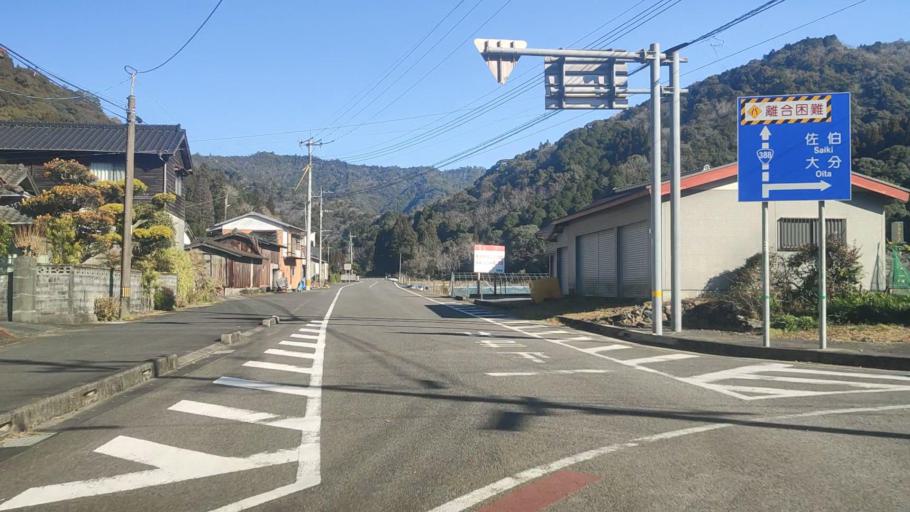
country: JP
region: Oita
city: Saiki
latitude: 32.7745
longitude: 131.8288
